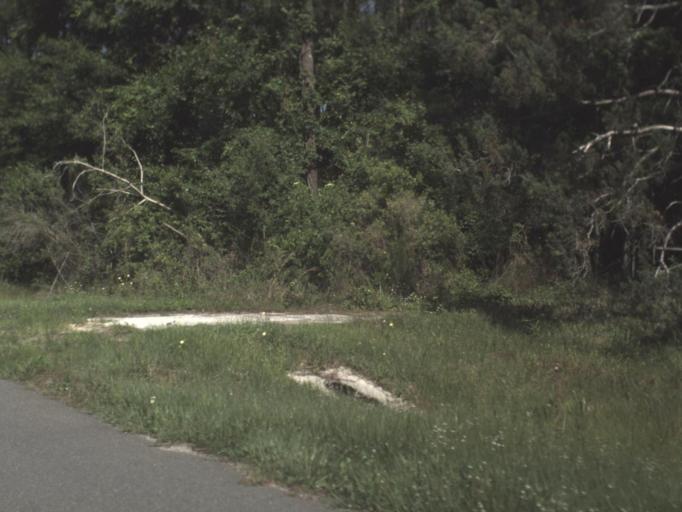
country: US
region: Florida
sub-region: Baker County
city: Macclenny
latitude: 30.2865
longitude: -82.0981
